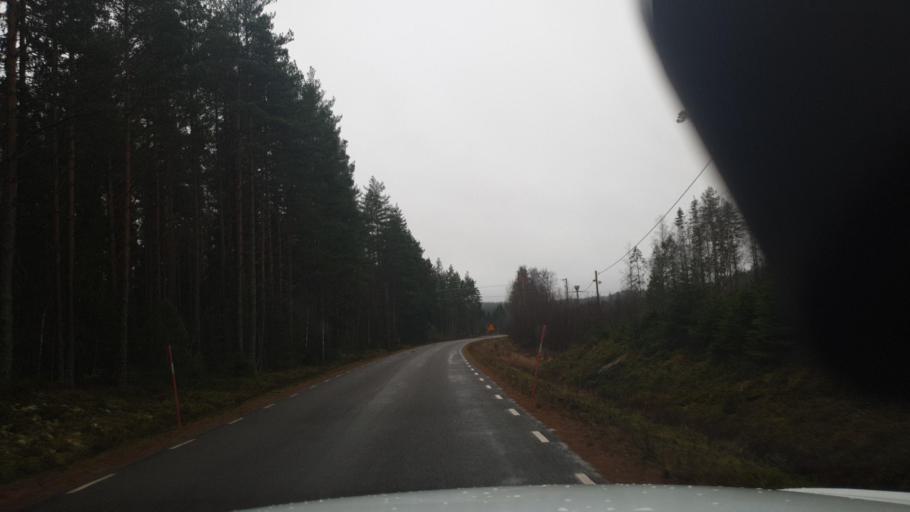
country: SE
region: Vaermland
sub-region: Eda Kommun
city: Amotfors
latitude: 59.5109
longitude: 12.3658
